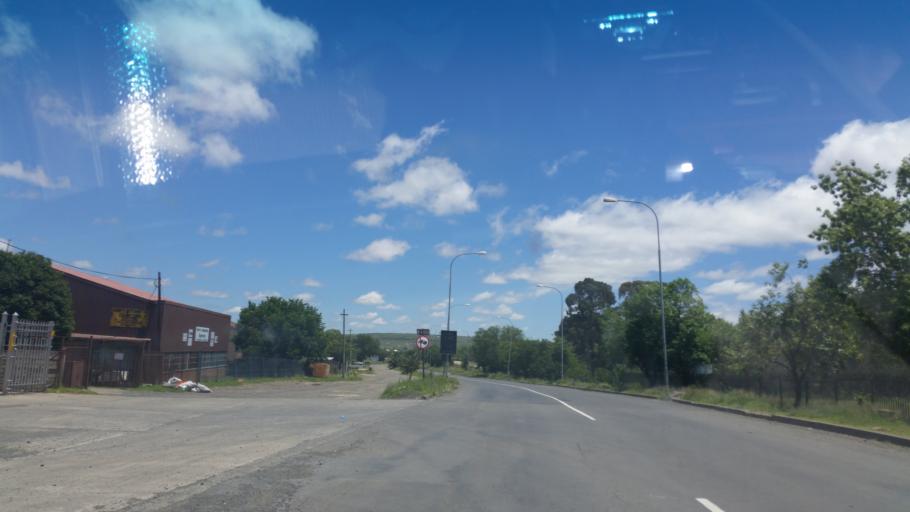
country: ZA
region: Orange Free State
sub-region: Thabo Mofutsanyana District Municipality
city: Harrismith
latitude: -28.2819
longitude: 29.1309
